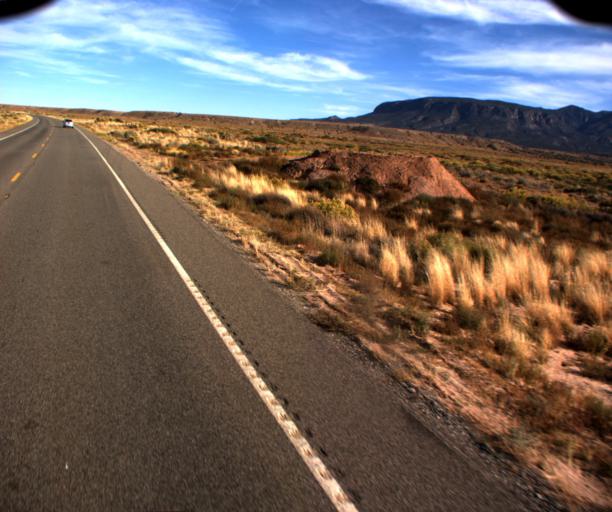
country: US
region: Arizona
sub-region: Apache County
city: Lukachukai
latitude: 36.9308
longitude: -109.2198
